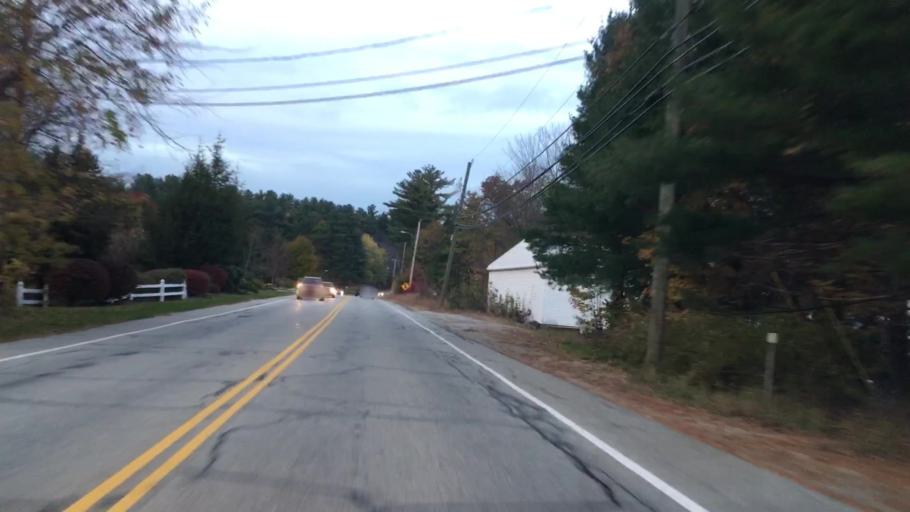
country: US
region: New Hampshire
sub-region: Hillsborough County
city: Milford
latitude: 42.8417
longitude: -71.6381
